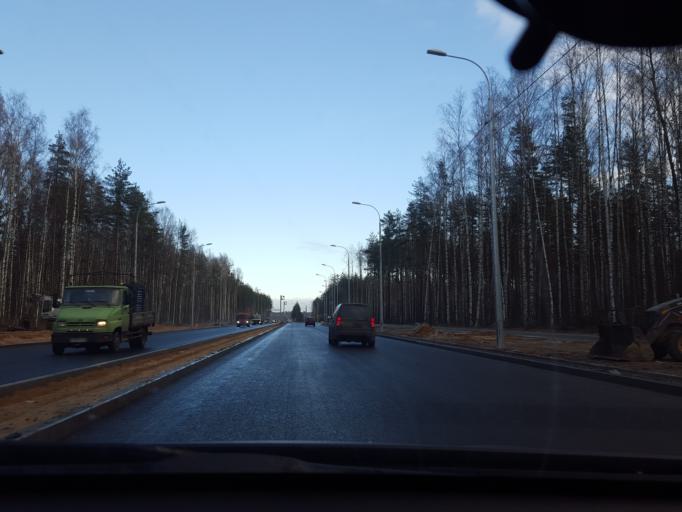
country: RU
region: St.-Petersburg
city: Pargolovo
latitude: 60.0590
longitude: 30.2454
